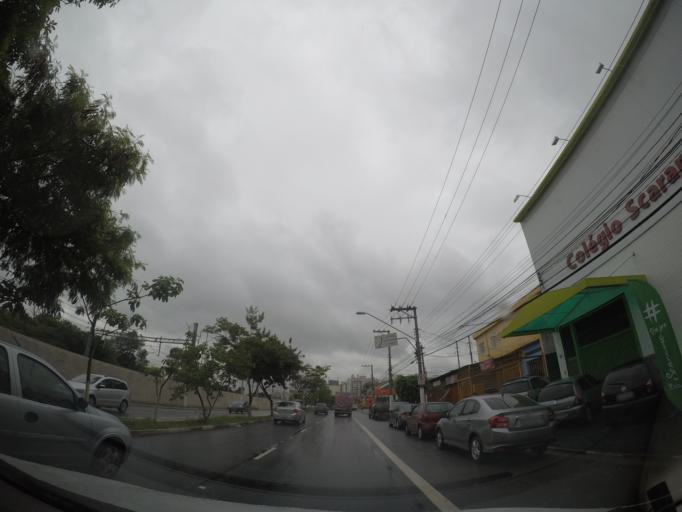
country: BR
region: Sao Paulo
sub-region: Guarulhos
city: Guarulhos
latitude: -23.4999
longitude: -46.5271
